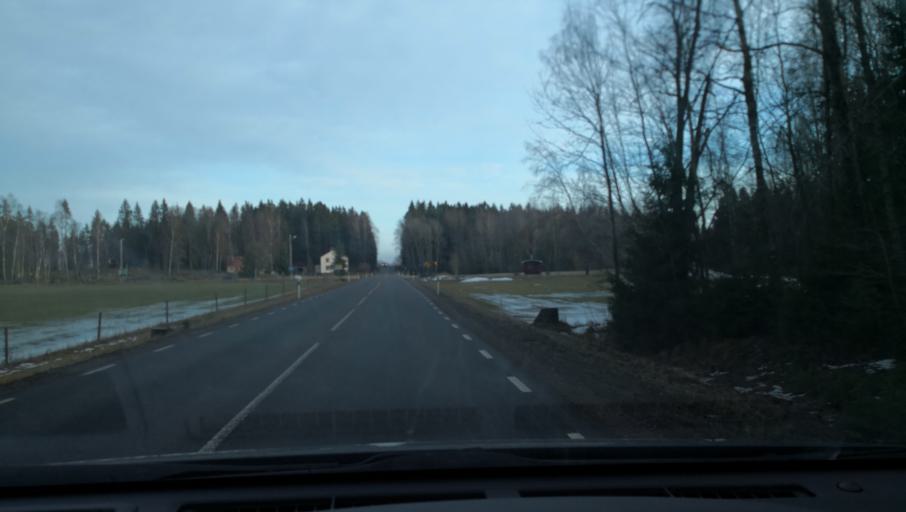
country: SE
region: Vaestra Goetaland
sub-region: Gullspangs Kommun
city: Gullspang
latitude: 59.0572
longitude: 14.2326
